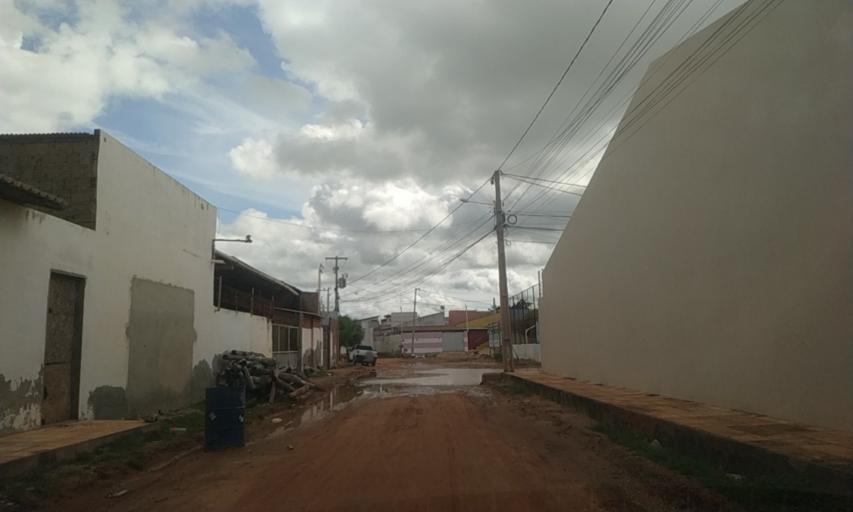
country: BR
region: Rio Grande do Norte
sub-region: Areia Branca
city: Areia Branca
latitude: -4.9536
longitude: -37.1221
